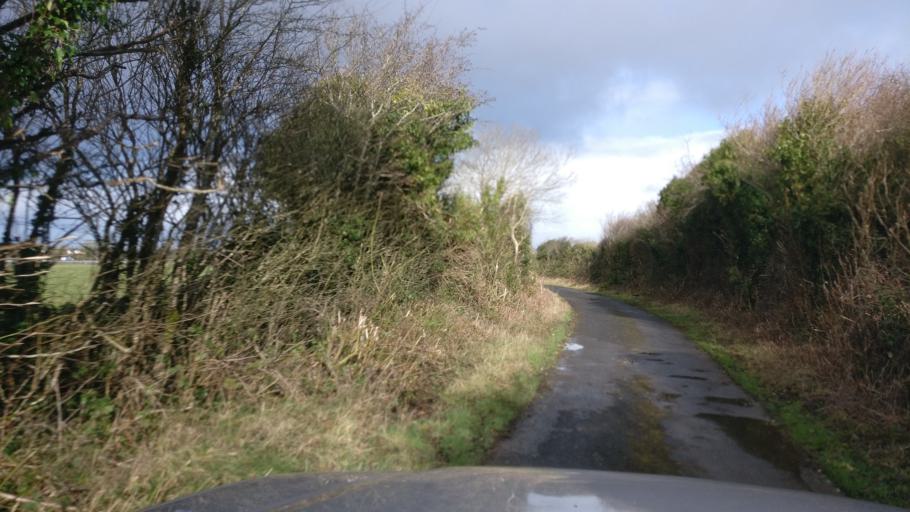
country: IE
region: Connaught
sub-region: County Galway
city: Oranmore
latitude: 53.2398
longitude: -8.8321
